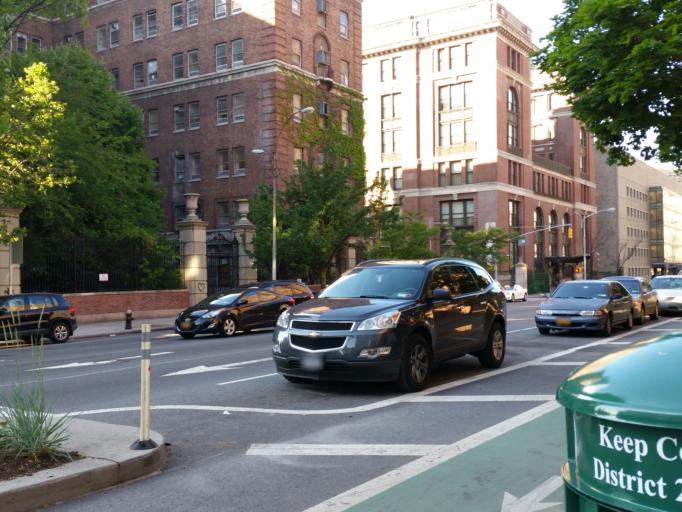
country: US
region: New York
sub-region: Queens County
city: Long Island City
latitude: 40.7418
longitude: -73.9758
